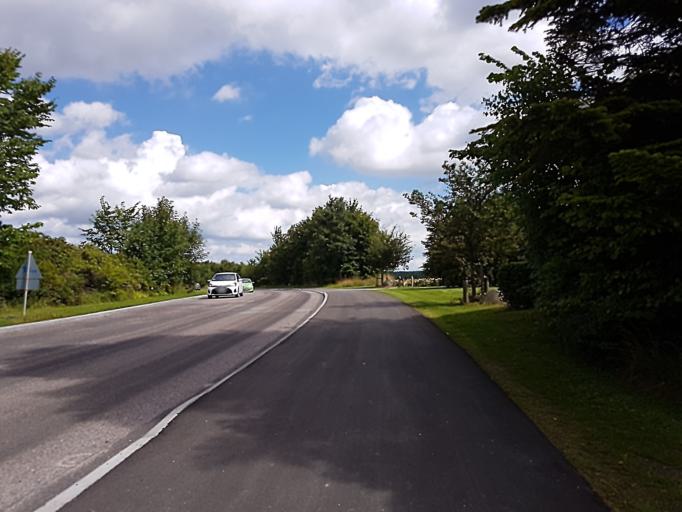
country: DK
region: Capital Region
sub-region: Egedal Kommune
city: Ganlose
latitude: 55.7957
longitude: 12.2734
